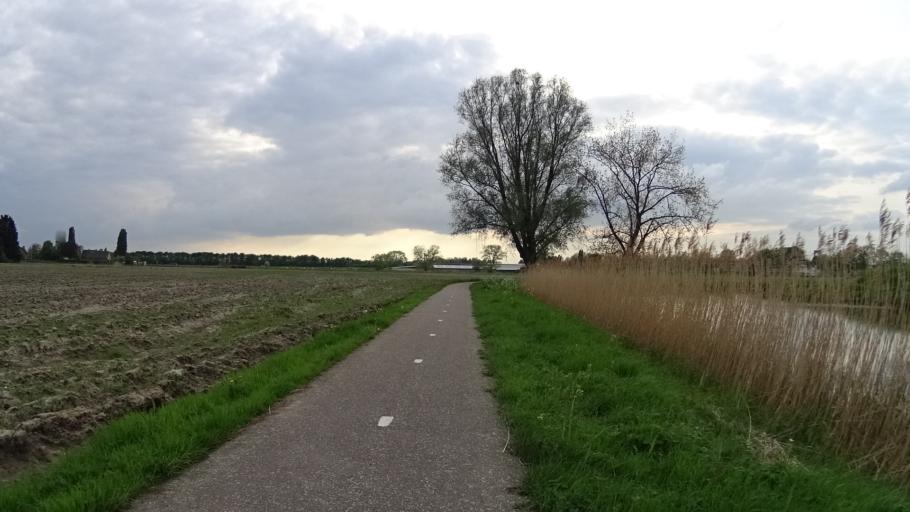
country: NL
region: North Brabant
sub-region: Gemeente Heusden
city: Heusden
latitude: 51.7297
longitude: 5.1317
